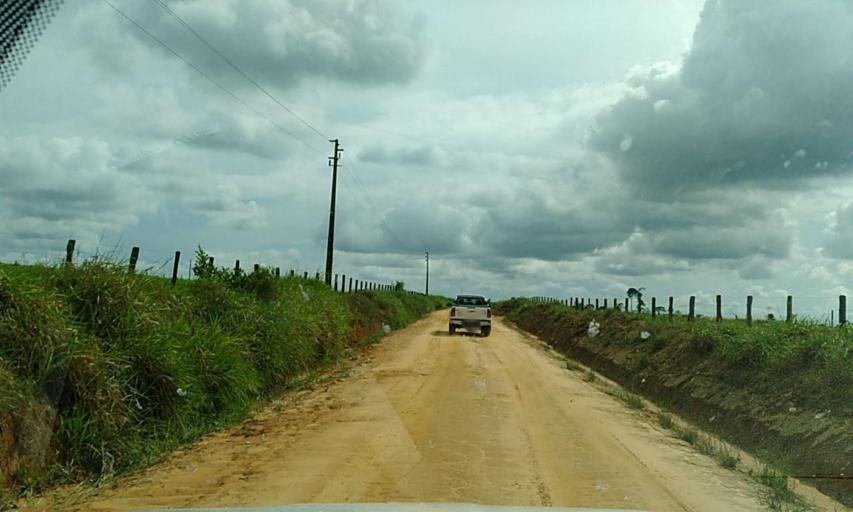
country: BR
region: Para
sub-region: Altamira
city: Altamira
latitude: -3.2543
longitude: -52.6944
